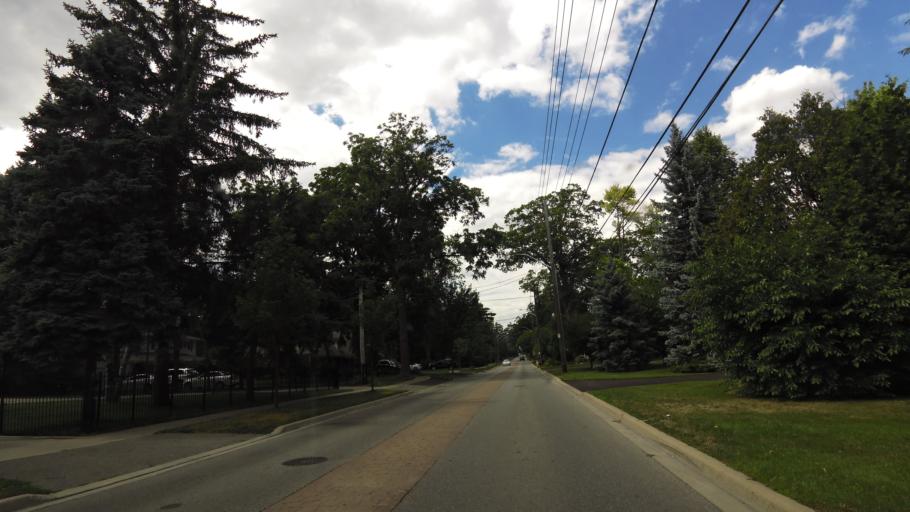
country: CA
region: Ontario
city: Mississauga
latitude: 43.5209
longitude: -79.6289
